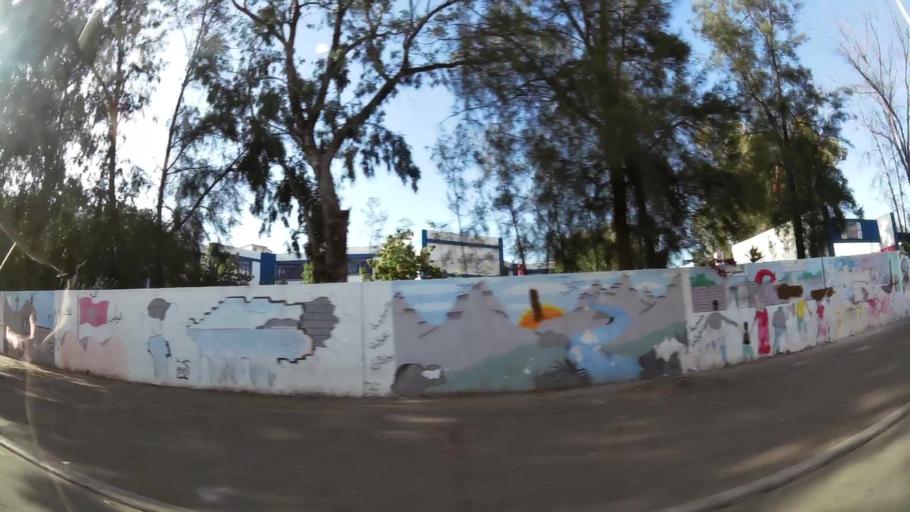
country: MA
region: Souss-Massa-Draa
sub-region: Agadir-Ida-ou-Tnan
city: Agadir
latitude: 30.4274
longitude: -9.5861
